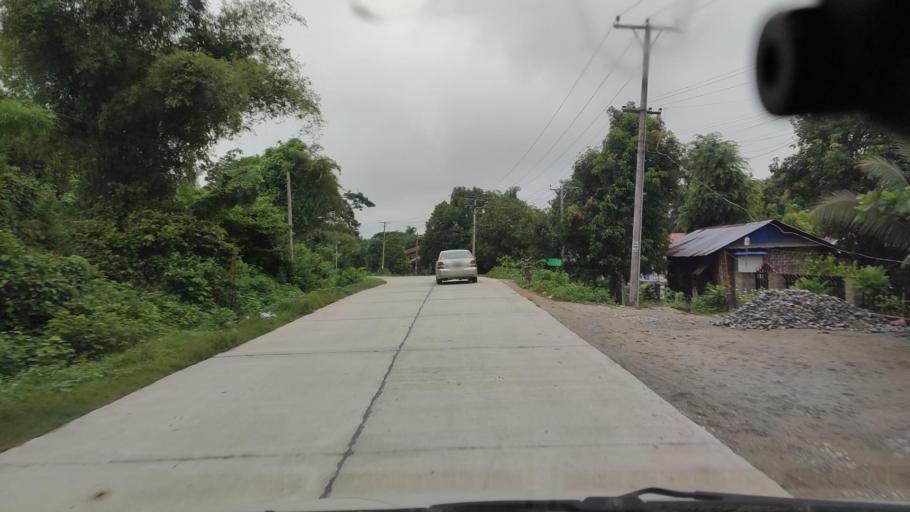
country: MM
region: Bago
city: Taungoo
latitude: 18.9635
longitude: 96.4870
